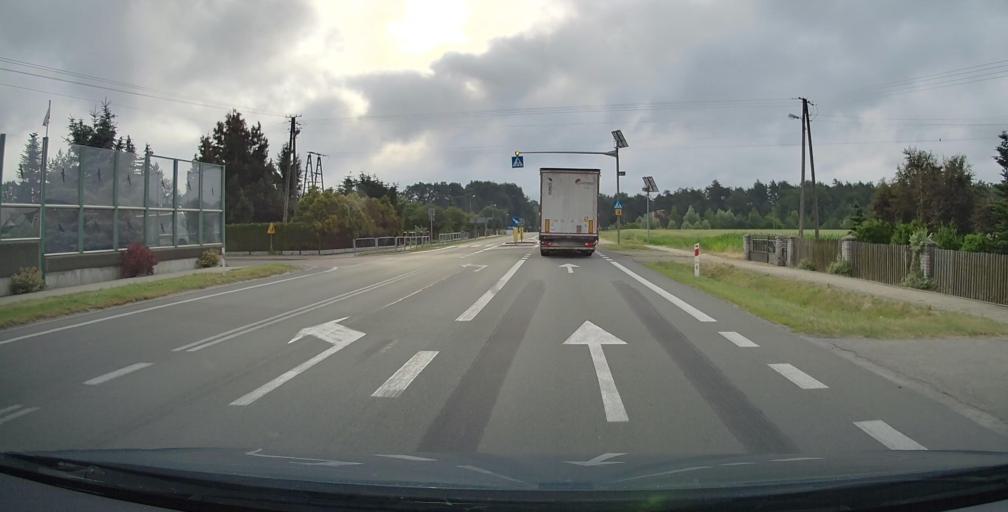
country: PL
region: Lublin Voivodeship
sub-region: Powiat lukowski
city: Trzebieszow
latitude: 52.0578
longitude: 22.6137
